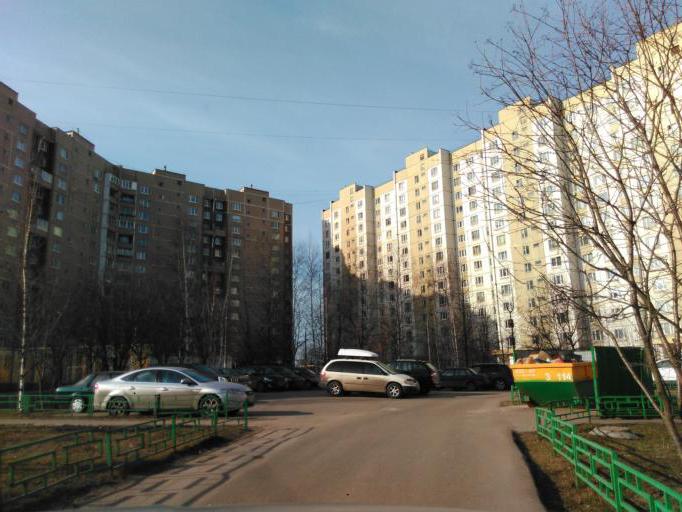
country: RU
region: Moskovskaya
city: Andreyevka
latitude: 55.9718
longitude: 37.1512
